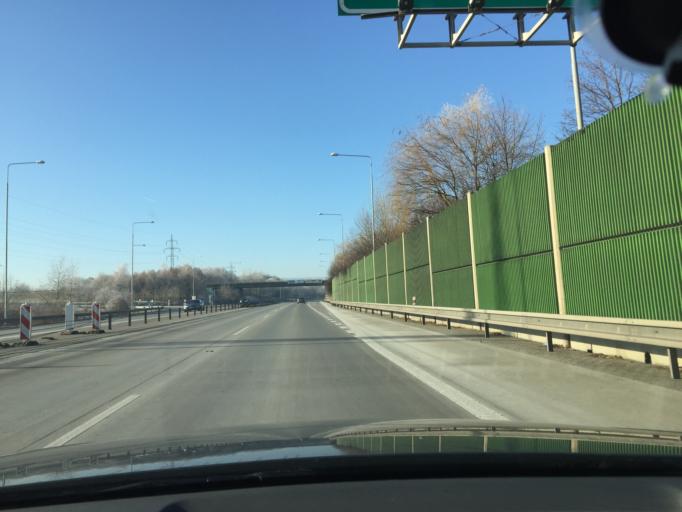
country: CZ
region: Central Bohemia
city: Trebotov
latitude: 50.0250
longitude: 14.3011
